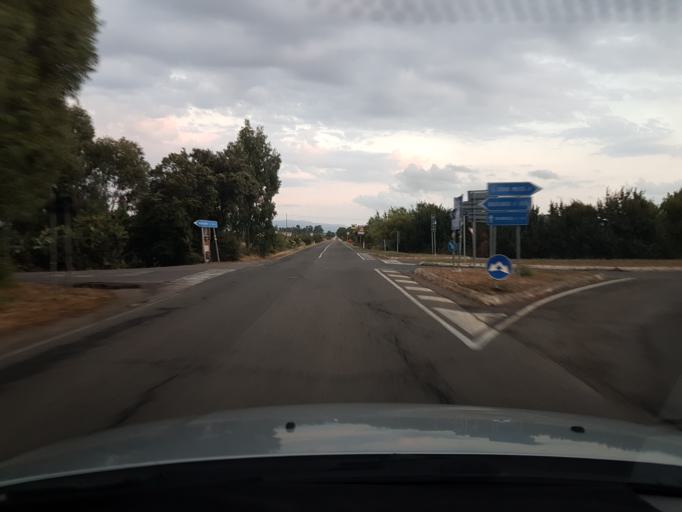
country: IT
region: Sardinia
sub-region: Provincia di Oristano
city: Milis
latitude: 40.0407
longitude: 8.6363
